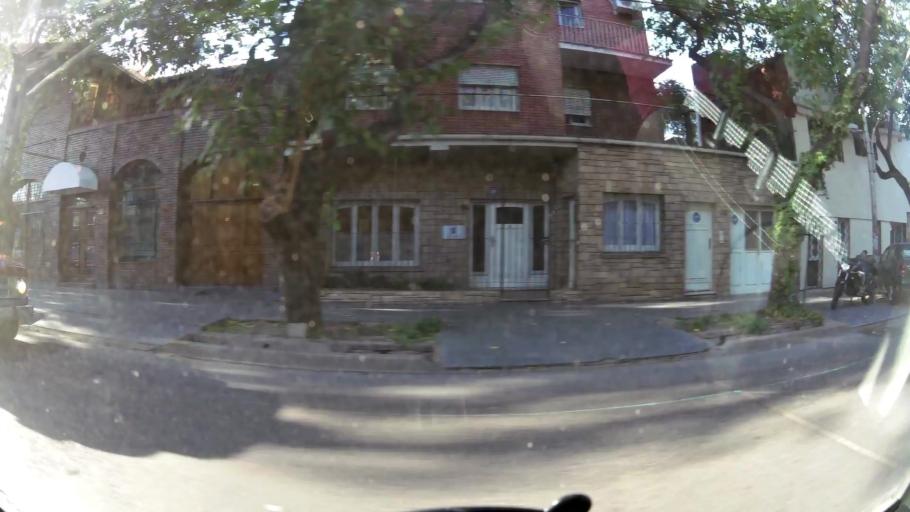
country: AR
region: Mendoza
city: Mendoza
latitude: -32.9036
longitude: -68.8469
